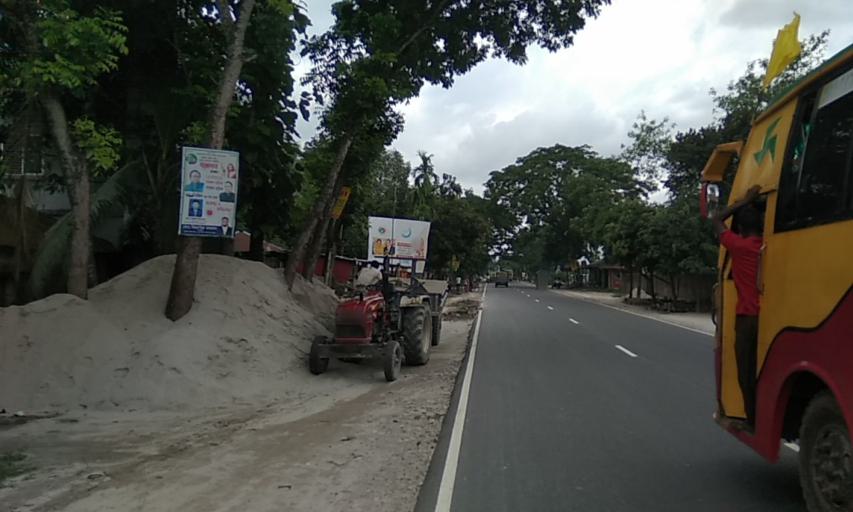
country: BD
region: Rangpur Division
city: Rangpur
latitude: 25.7980
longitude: 89.1938
